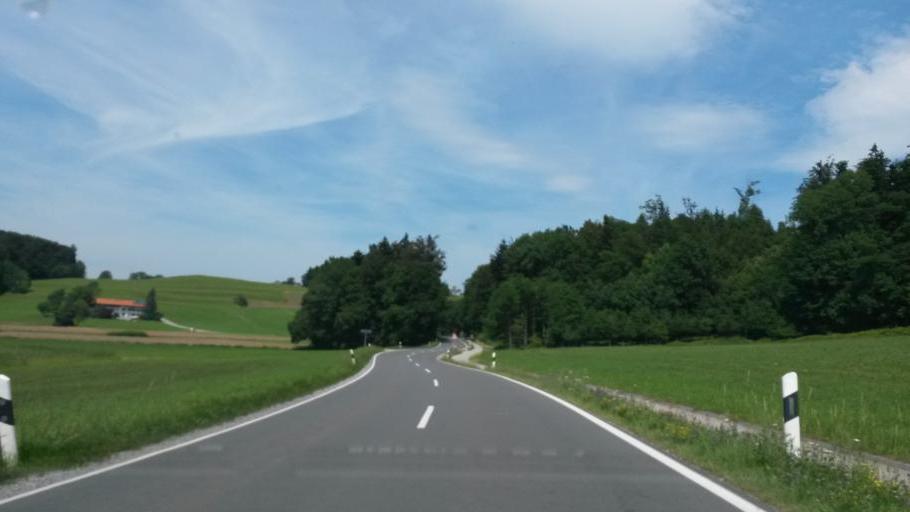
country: DE
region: Bavaria
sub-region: Upper Bavaria
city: Aschau im Chiemgau
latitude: 47.7928
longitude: 12.3431
